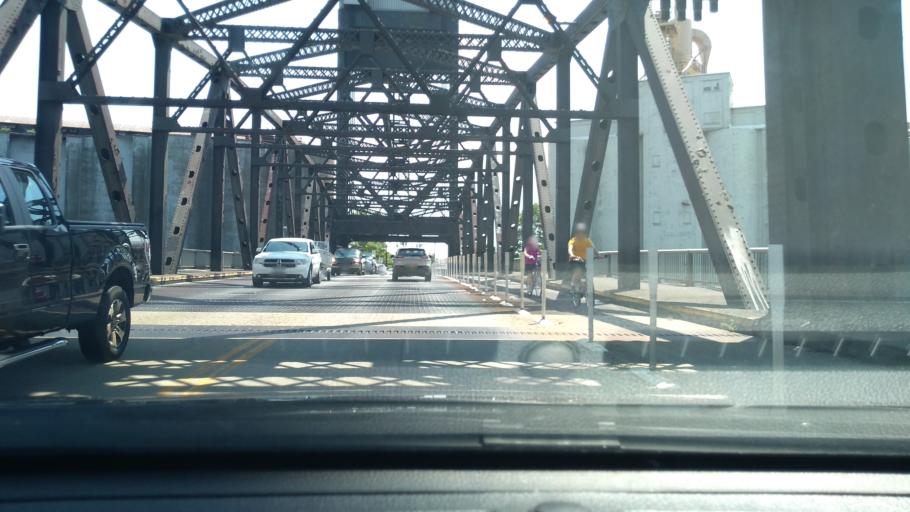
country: US
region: New York
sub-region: Erie County
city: Buffalo
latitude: 42.8623
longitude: -78.8674
